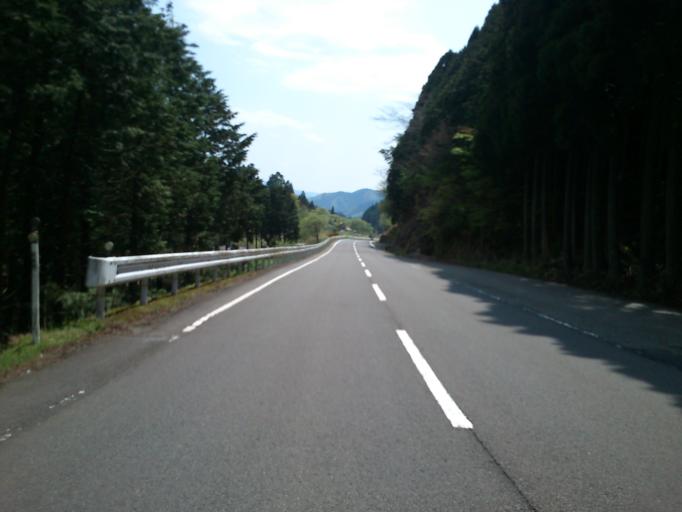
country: JP
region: Hyogo
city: Toyooka
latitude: 35.4035
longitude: 134.9487
